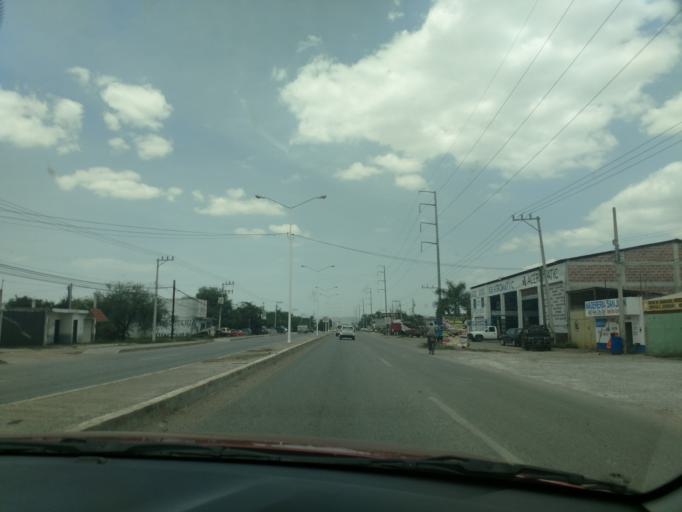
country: MX
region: San Luis Potosi
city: Rio Verde
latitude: 21.9221
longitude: -99.9736
